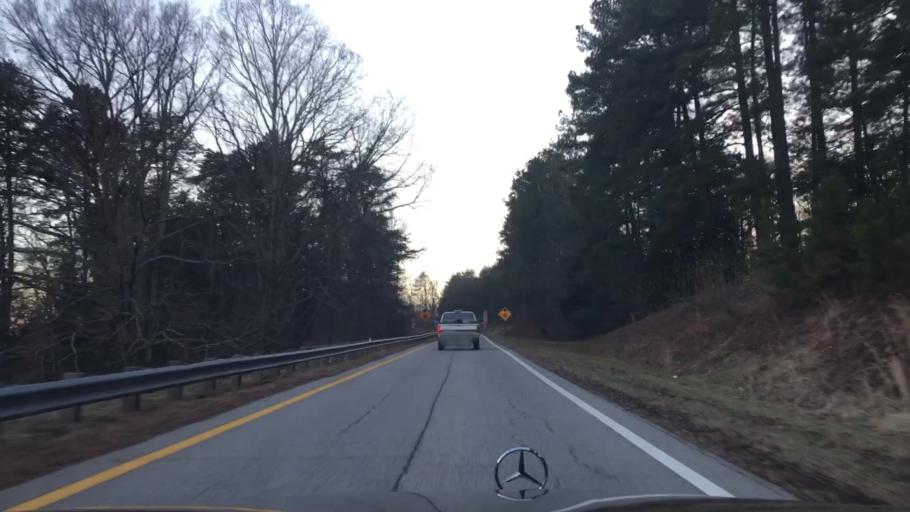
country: US
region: Virginia
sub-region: Pittsylvania County
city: Hurt
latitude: 37.1168
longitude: -79.3260
